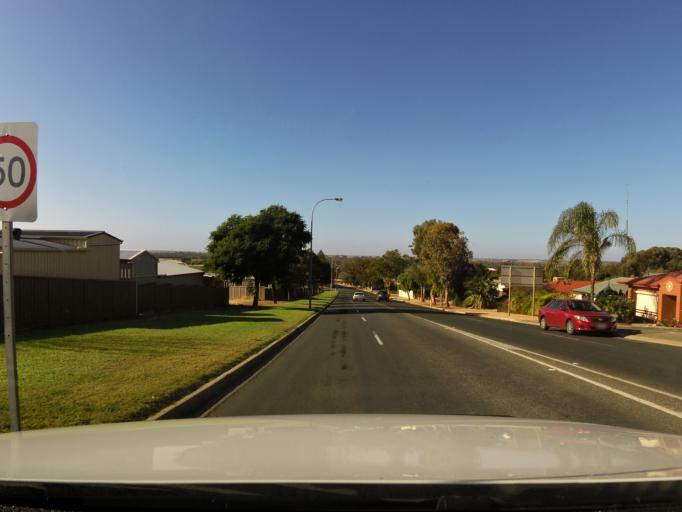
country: AU
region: South Australia
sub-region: Berri and Barmera
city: Berri
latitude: -34.2732
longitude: 140.6073
